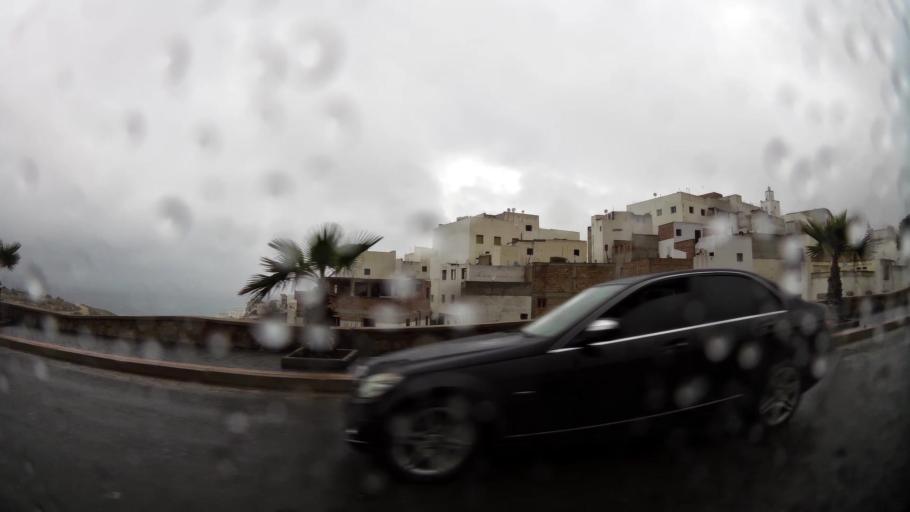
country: MA
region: Taza-Al Hoceima-Taounate
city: Al Hoceima
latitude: 35.2470
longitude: -3.9475
